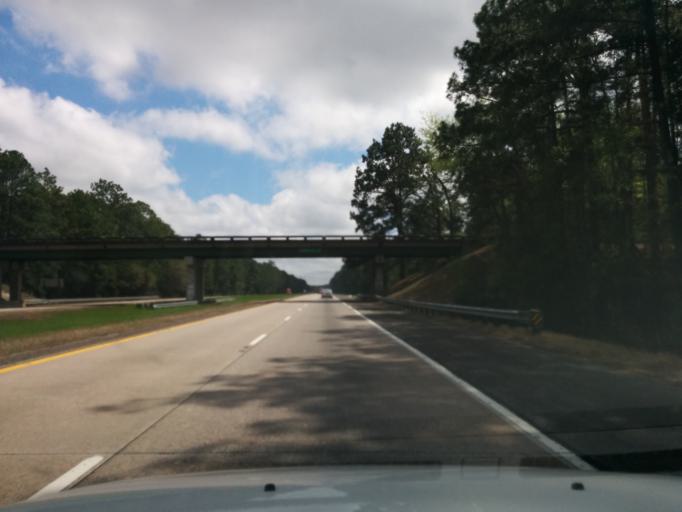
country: US
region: Georgia
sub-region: Chatham County
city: Bloomingdale
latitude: 32.1601
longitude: -81.4336
